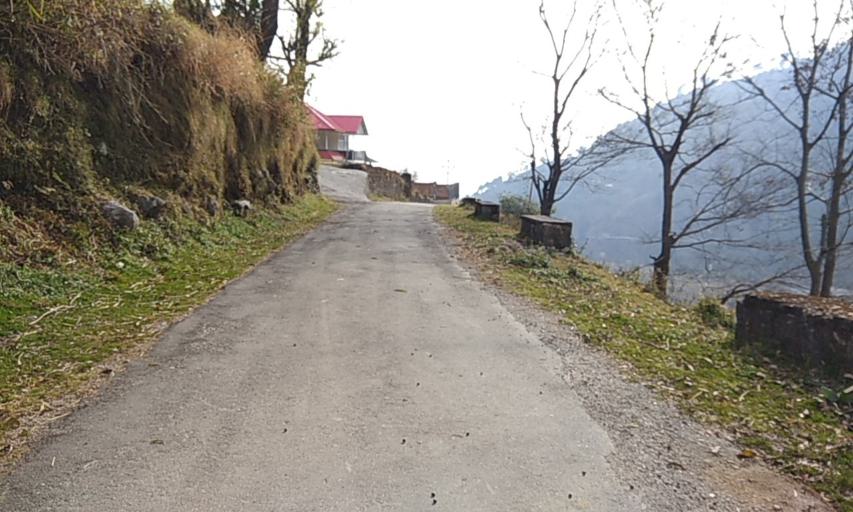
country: IN
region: Himachal Pradesh
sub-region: Kangra
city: Palampur
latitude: 32.1398
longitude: 76.5377
